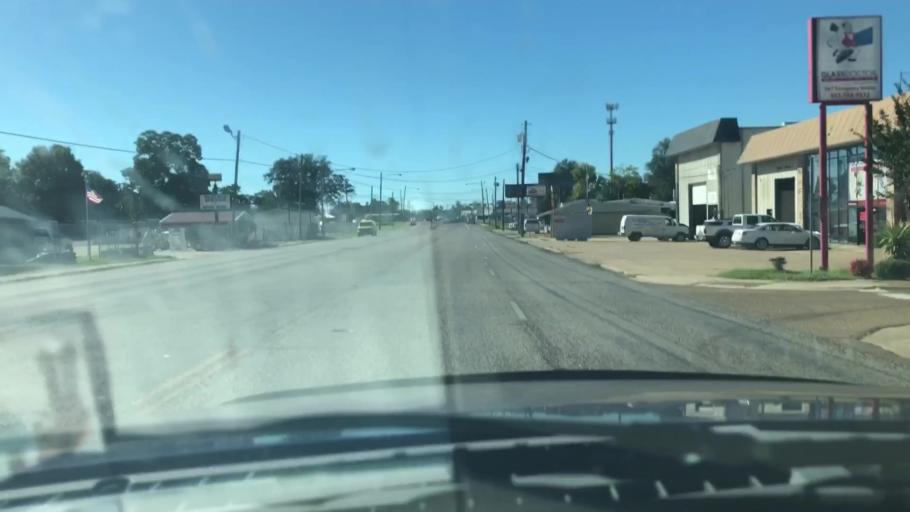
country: US
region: Texas
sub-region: Bowie County
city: Texarkana
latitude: 33.4374
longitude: -94.0532
